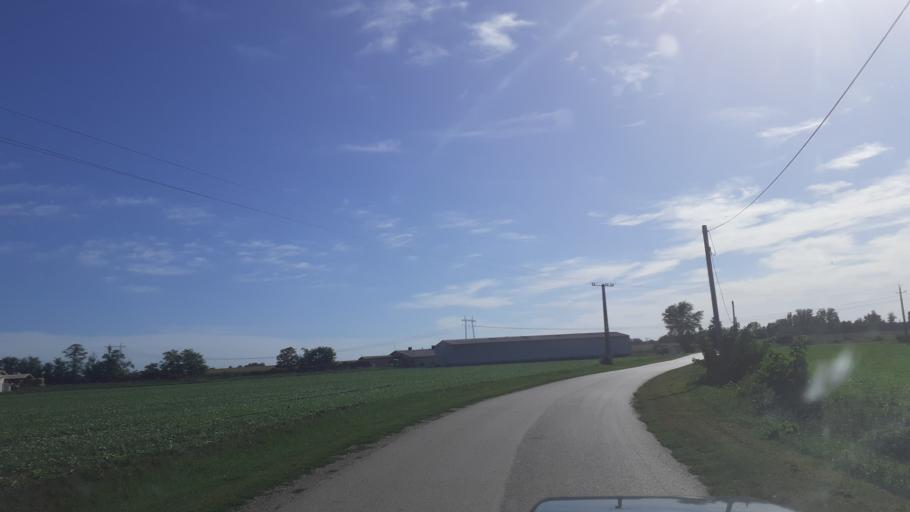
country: HU
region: Fejer
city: Pusztaszabolcs
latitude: 47.1935
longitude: 18.7612
